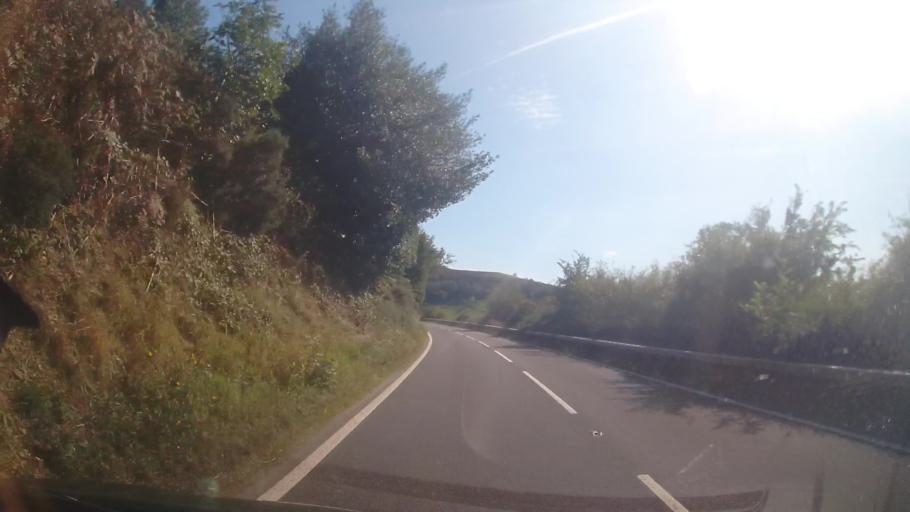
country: GB
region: Wales
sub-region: Sir Powys
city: Mochdre
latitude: 52.4556
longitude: -3.3478
